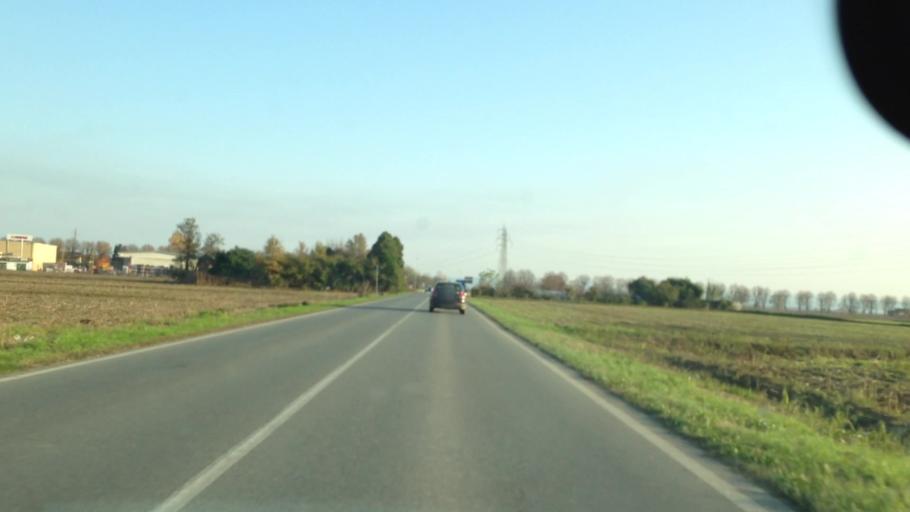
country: IT
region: Piedmont
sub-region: Provincia di Vercelli
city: Livorno Ferraris
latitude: 45.2763
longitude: 8.0726
